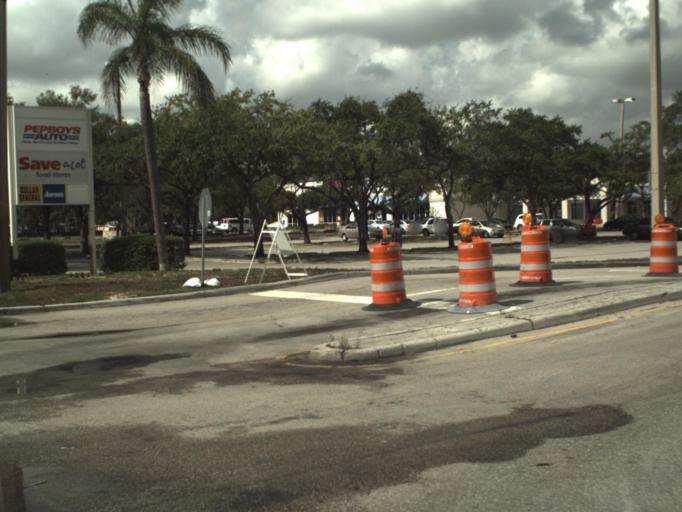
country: US
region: Florida
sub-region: Broward County
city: Pembroke Pines
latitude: 26.0047
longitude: -80.2075
